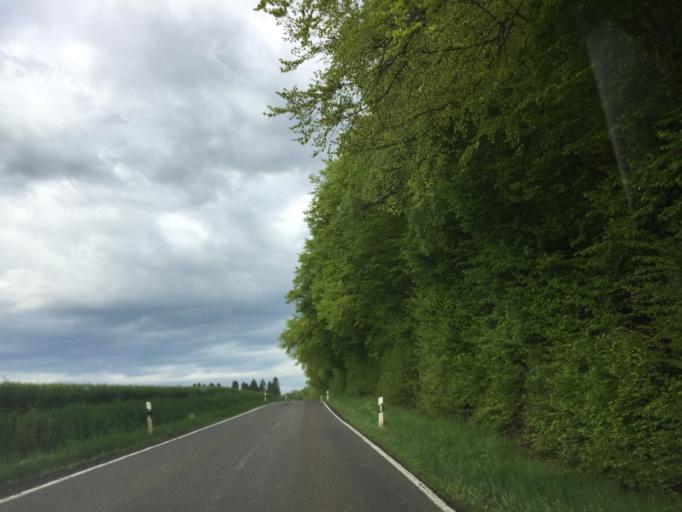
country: DE
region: Rheinland-Pfalz
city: Kammerforst
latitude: 50.4781
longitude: 7.6812
